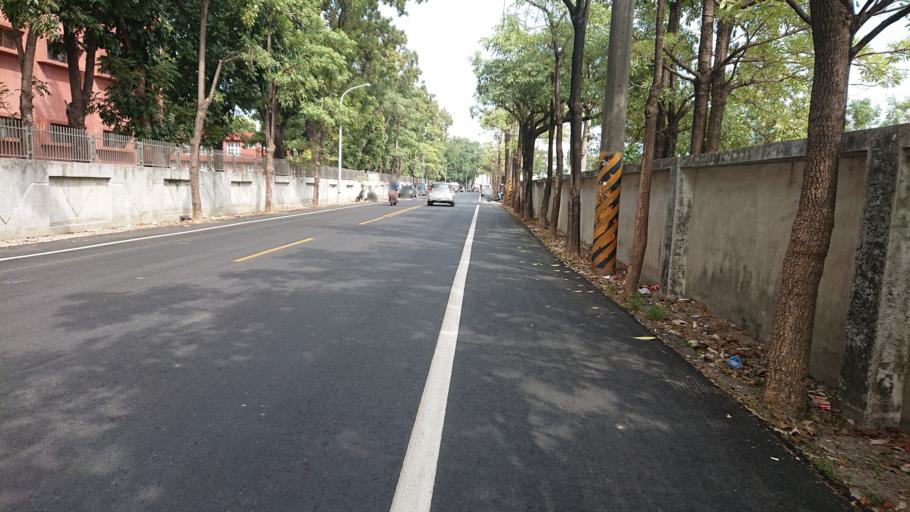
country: TW
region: Taiwan
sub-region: Tainan
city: Tainan
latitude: 23.0213
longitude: 120.2554
